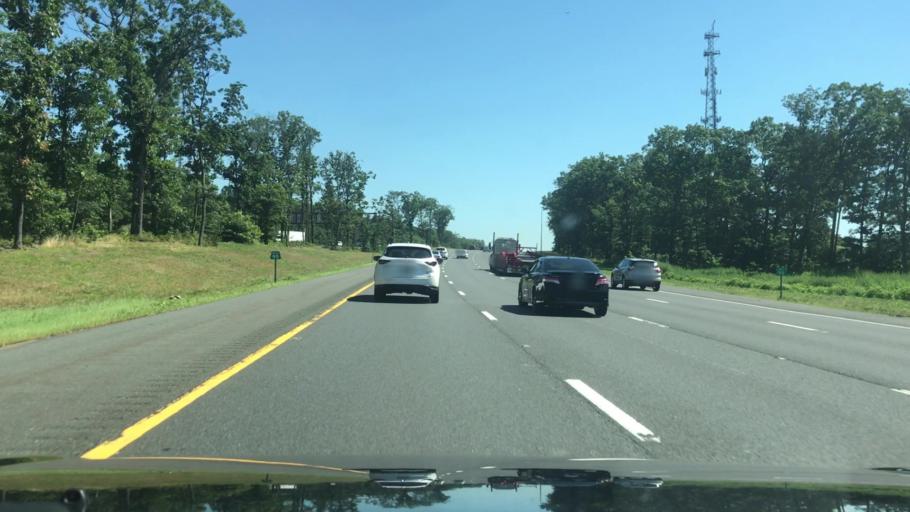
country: US
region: New Jersey
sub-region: Monmouth County
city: Ramtown
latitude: 40.1285
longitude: -74.1244
